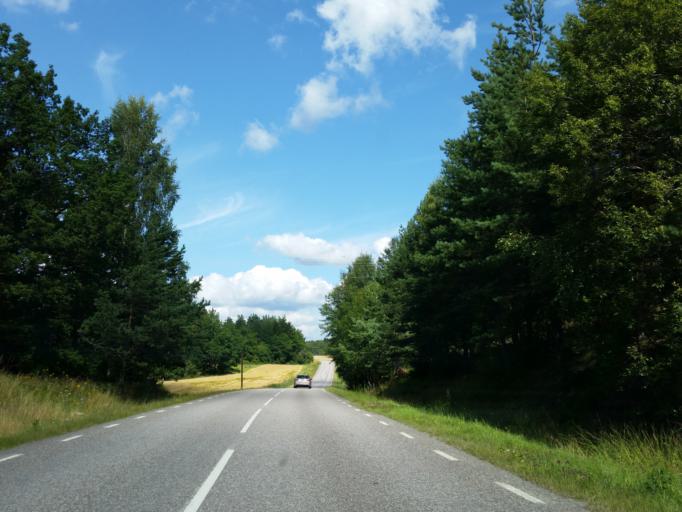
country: SE
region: Stockholm
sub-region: Sodertalje Kommun
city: Pershagen
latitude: 59.0137
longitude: 17.6648
